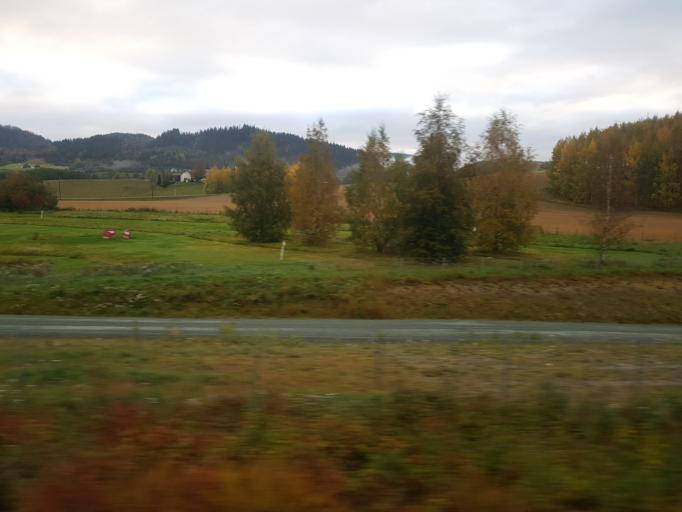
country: NO
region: Sor-Trondelag
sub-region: Melhus
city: Lundamo
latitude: 63.1968
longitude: 10.3040
